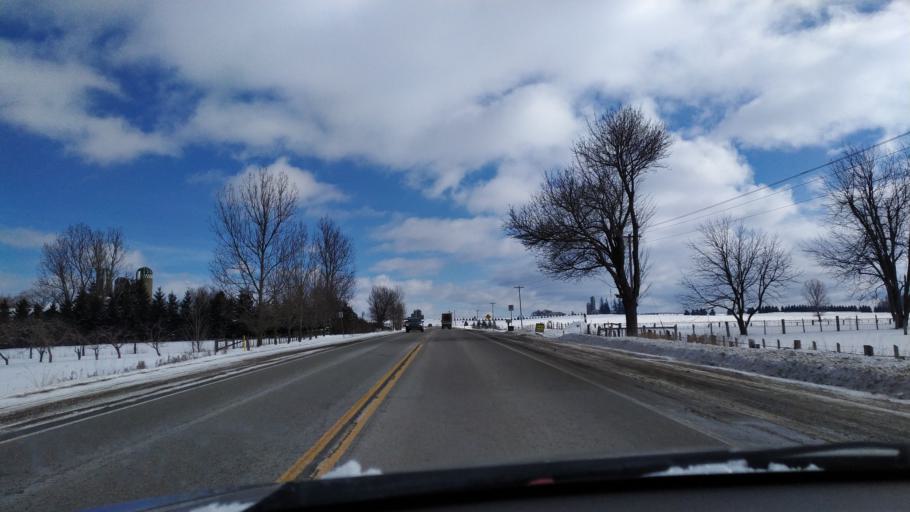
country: CA
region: Ontario
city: Waterloo
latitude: 43.5935
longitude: -80.6190
